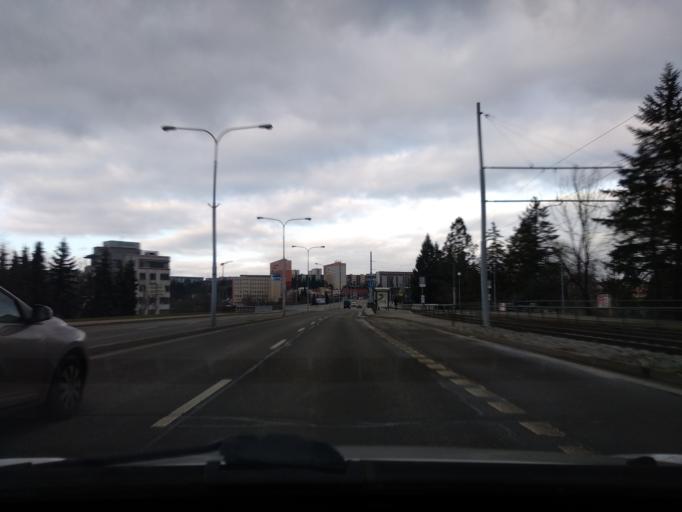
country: CZ
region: South Moravian
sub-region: Mesto Brno
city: Brno
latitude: 49.2195
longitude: 16.6187
